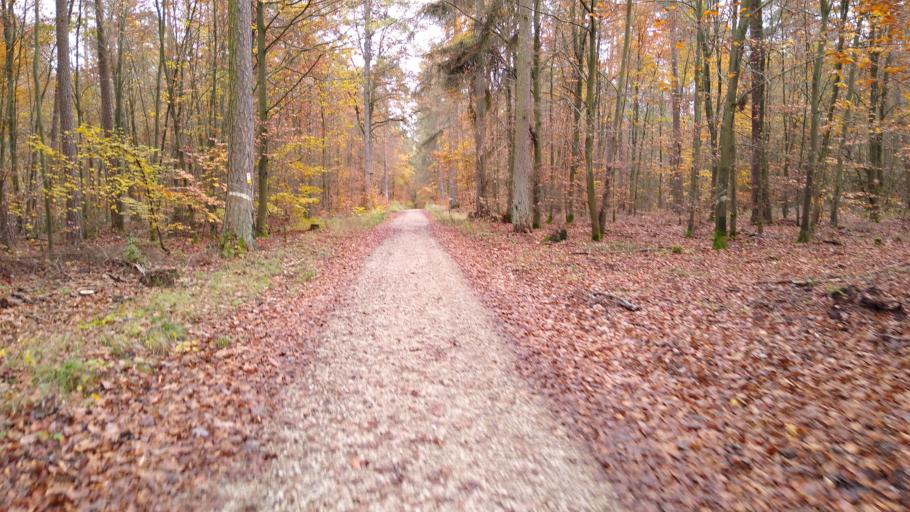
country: DE
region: Bavaria
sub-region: Regierungsbezirk Mittelfranken
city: Kalchreuth
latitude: 49.5440
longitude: 11.1179
